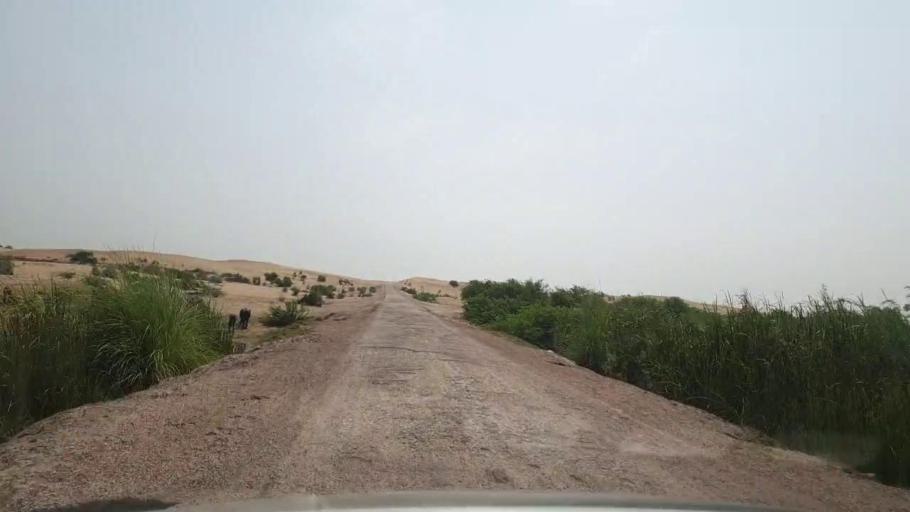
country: PK
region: Sindh
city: Rohri
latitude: 27.6179
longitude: 69.1137
